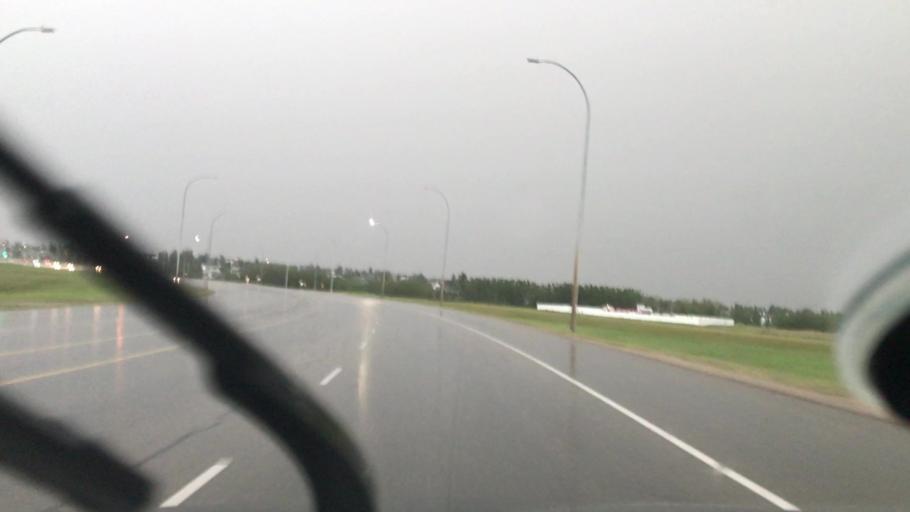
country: CA
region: Alberta
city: Devon
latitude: 53.4457
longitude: -113.5958
